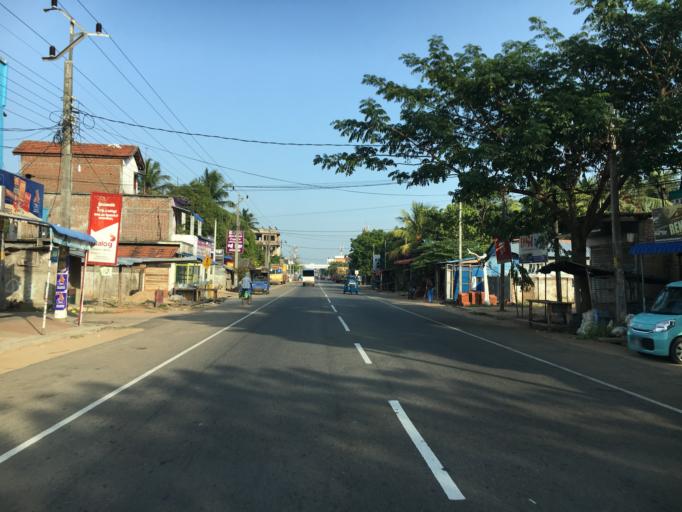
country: LK
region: Eastern Province
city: Eravur Town
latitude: 7.9118
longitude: 81.5278
